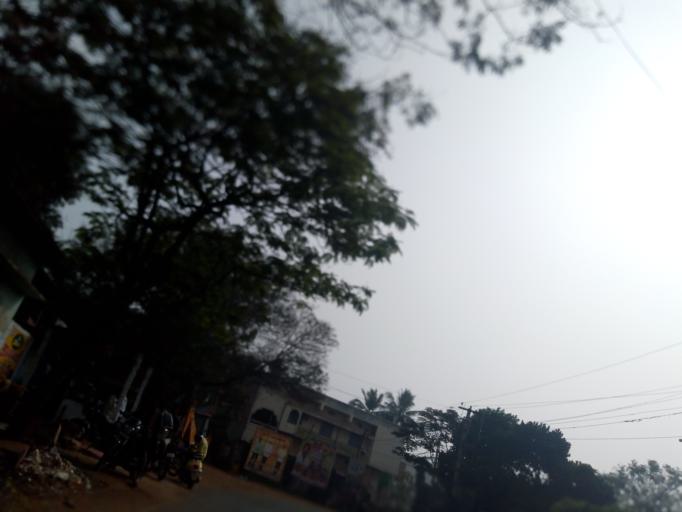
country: IN
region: Andhra Pradesh
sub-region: West Godavari
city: Tadepallegudem
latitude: 16.8173
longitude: 81.4057
